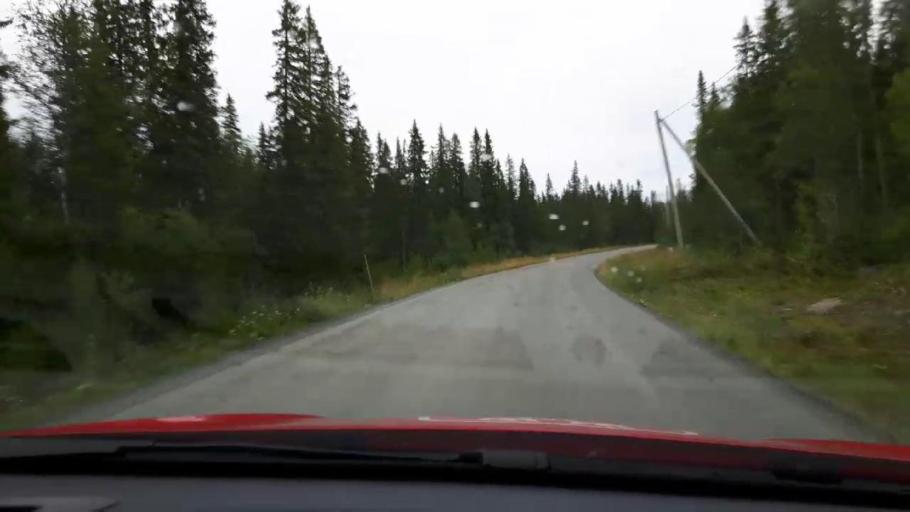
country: SE
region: Jaemtland
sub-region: Are Kommun
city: Jarpen
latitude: 63.4308
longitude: 13.3070
